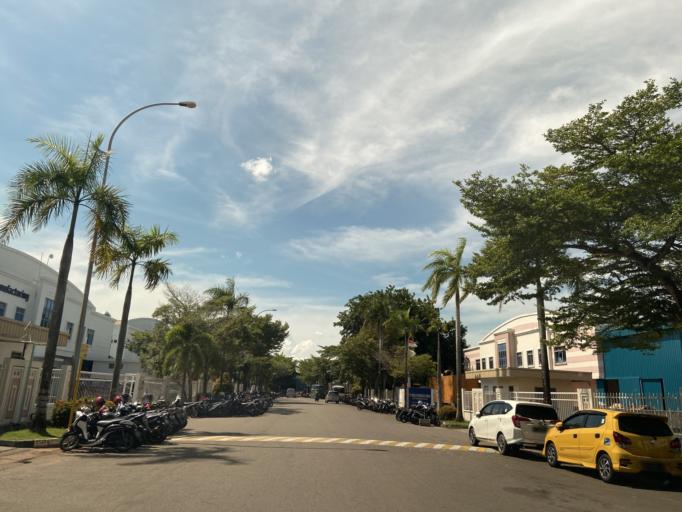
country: SG
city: Singapore
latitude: 1.1091
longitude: 104.0637
